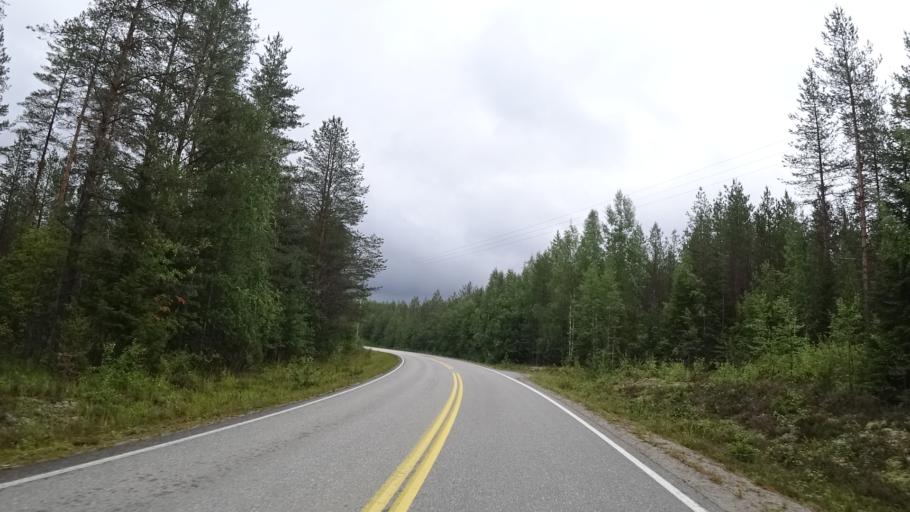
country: FI
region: North Karelia
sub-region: Joensuu
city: Ilomantsi
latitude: 63.2504
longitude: 30.7120
